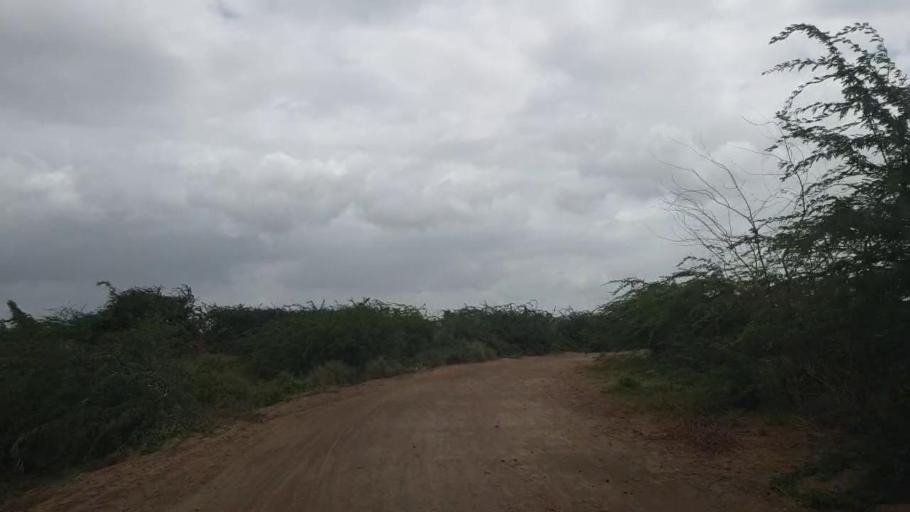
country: PK
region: Sindh
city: Badin
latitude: 24.6400
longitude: 68.9485
